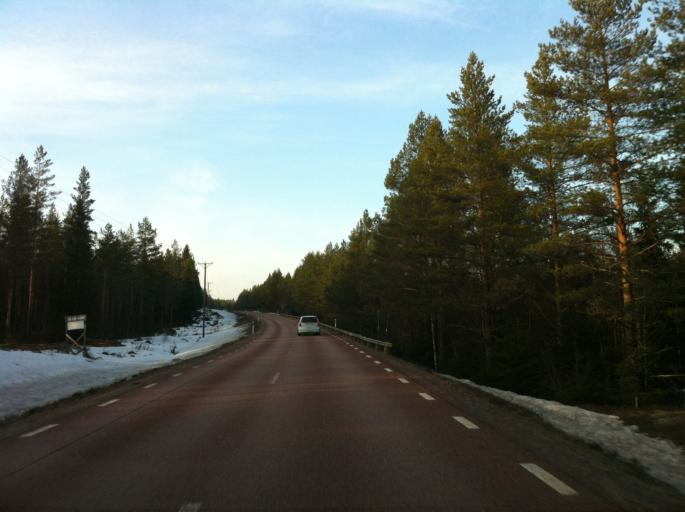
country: SE
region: Vaermland
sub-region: Filipstads Kommun
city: Lesjofors
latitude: 60.1760
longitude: 14.1977
